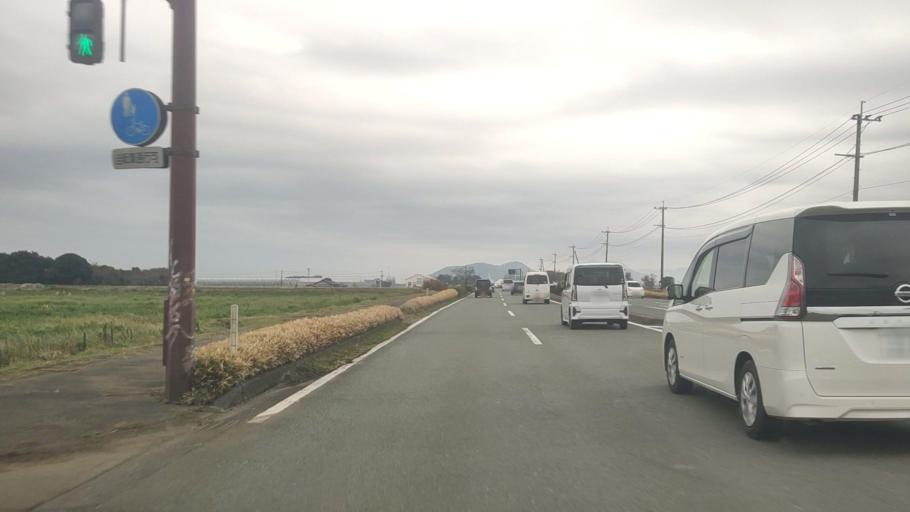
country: JP
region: Kumamoto
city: Ozu
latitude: 32.8459
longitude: 130.8305
